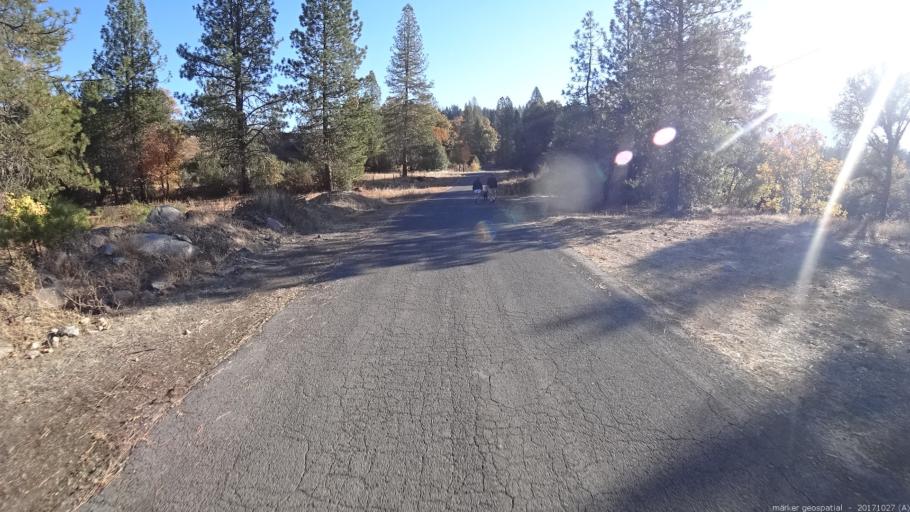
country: US
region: California
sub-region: Shasta County
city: Burney
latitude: 41.0221
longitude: -121.9080
